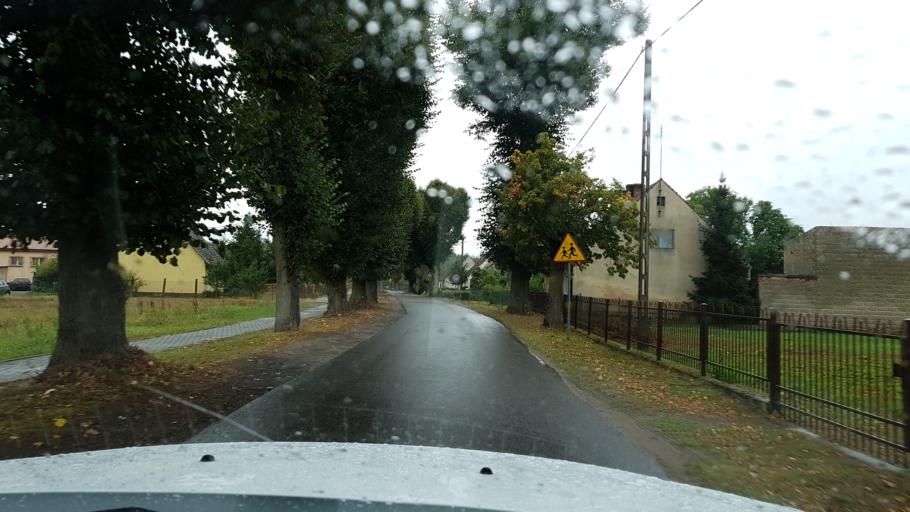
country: DE
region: Brandenburg
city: Schoneberg
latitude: 52.9763
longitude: 14.2071
